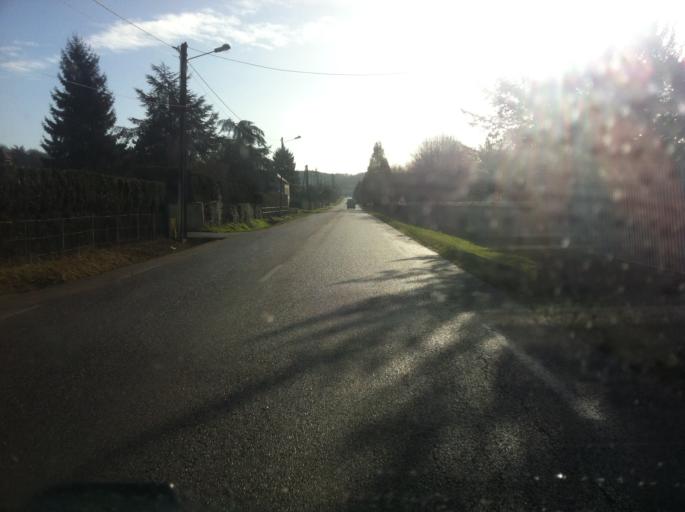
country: FR
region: Haute-Normandie
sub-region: Departement de la Seine-Maritime
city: Saint-Martin-de-Boscherville
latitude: 49.4593
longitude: 0.9579
